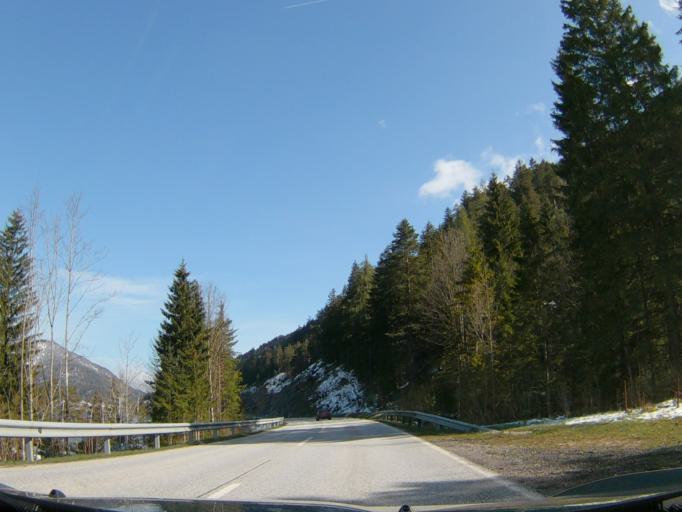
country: AT
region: Tyrol
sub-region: Politischer Bezirk Schwaz
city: Achenkirch
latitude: 47.4894
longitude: 11.7146
